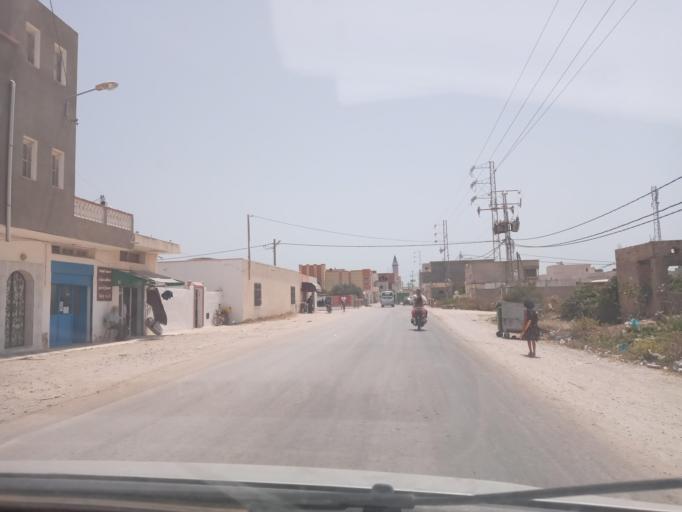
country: TN
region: Nabul
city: El Haouaria
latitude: 37.0135
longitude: 10.9518
